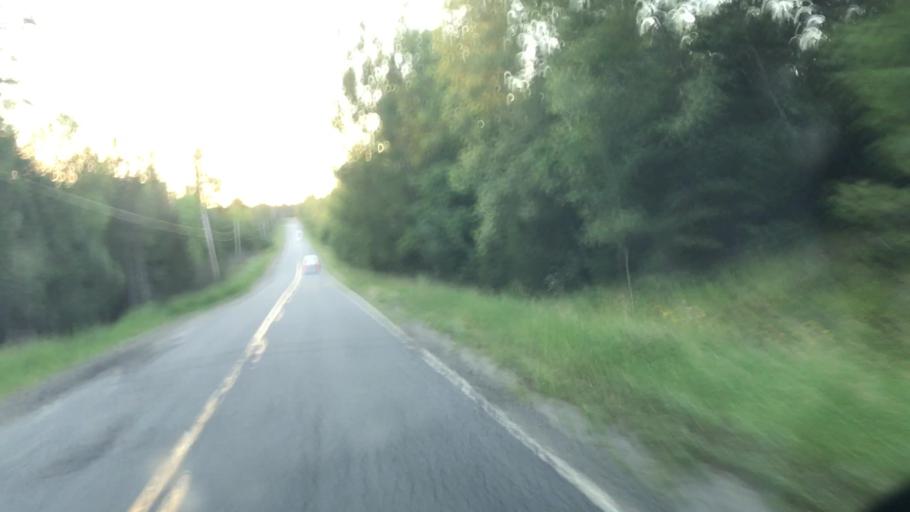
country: US
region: Maine
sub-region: Penobscot County
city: Medway
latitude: 45.6007
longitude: -68.2489
